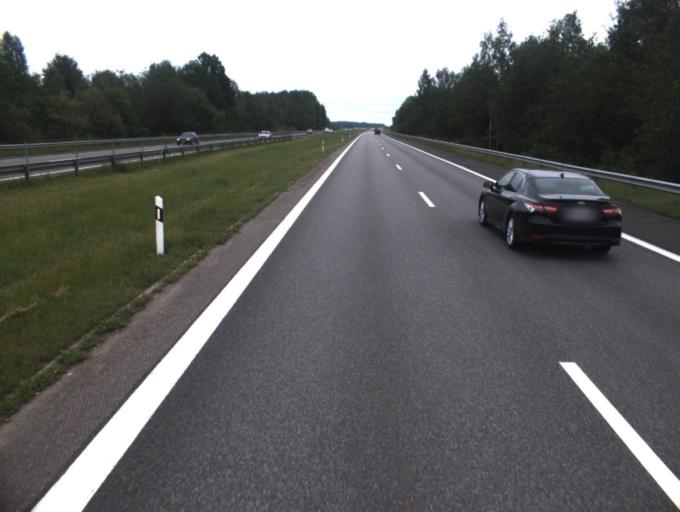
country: LT
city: Ariogala
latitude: 55.2762
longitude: 23.3594
